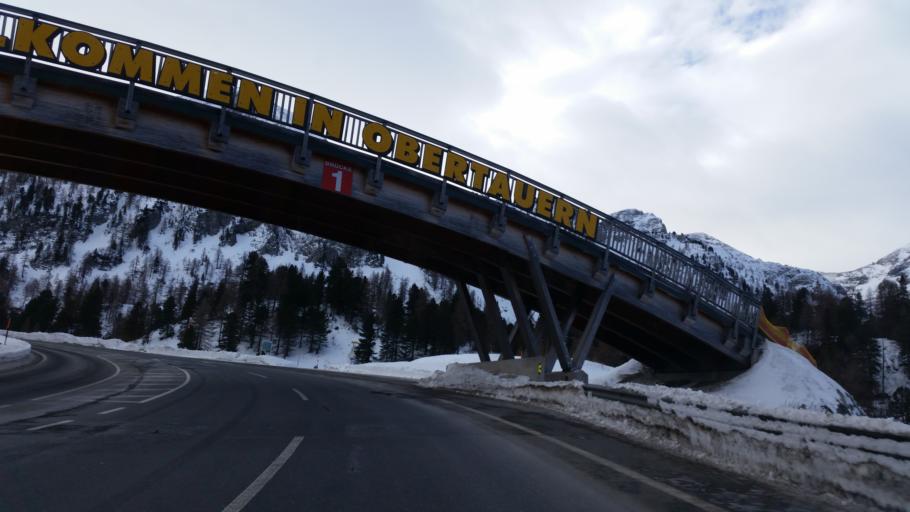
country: AT
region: Salzburg
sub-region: Politischer Bezirk Sankt Johann im Pongau
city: Untertauern
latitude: 47.2523
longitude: 13.5255
